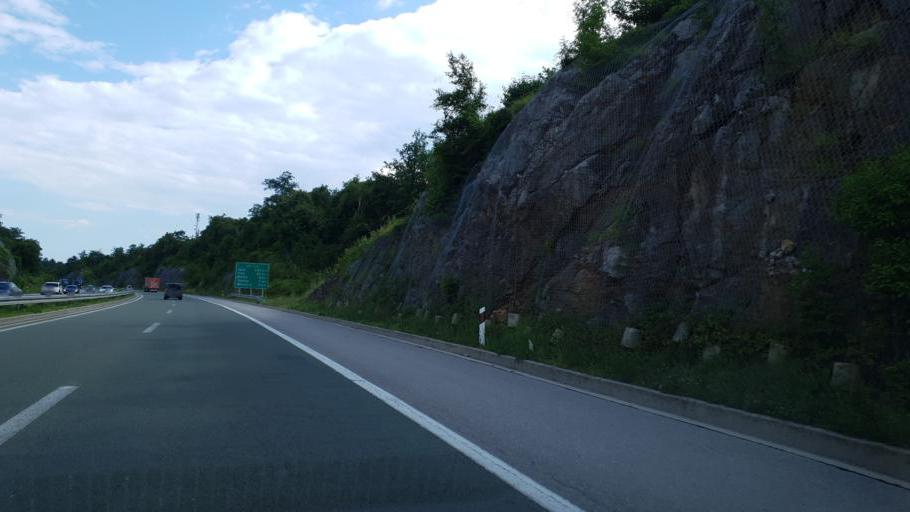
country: HR
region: Primorsko-Goranska
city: Matulji
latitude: 45.3882
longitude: 14.3007
